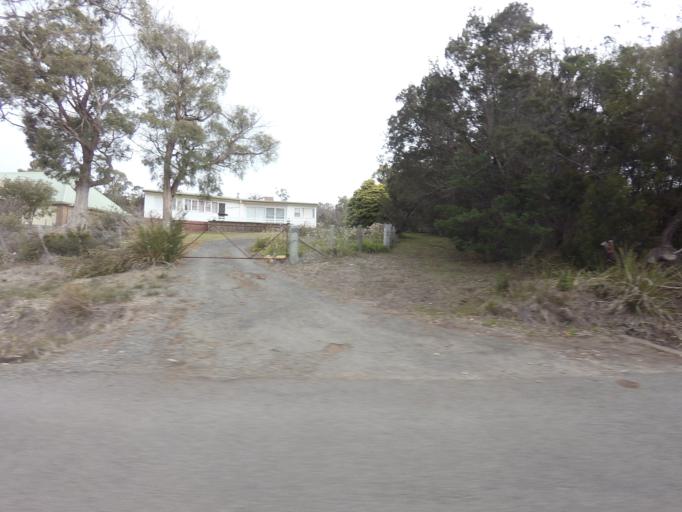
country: AU
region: Tasmania
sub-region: Sorell
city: Sorell
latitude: -42.5312
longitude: 147.9098
